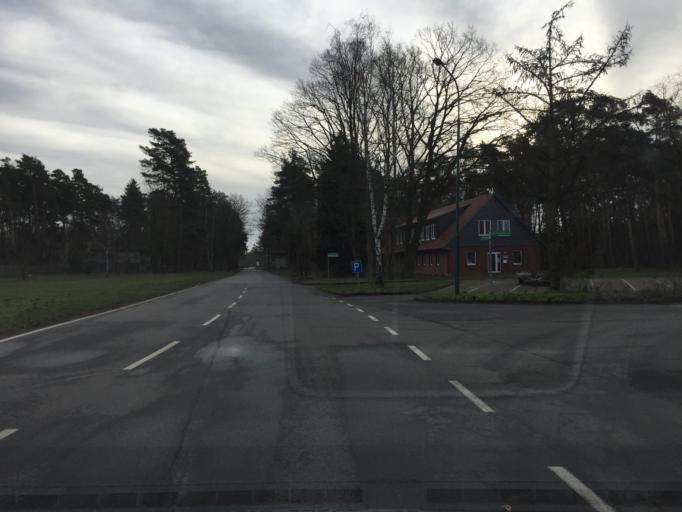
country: DE
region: Lower Saxony
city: Leese
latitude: 52.5255
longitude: 9.1317
